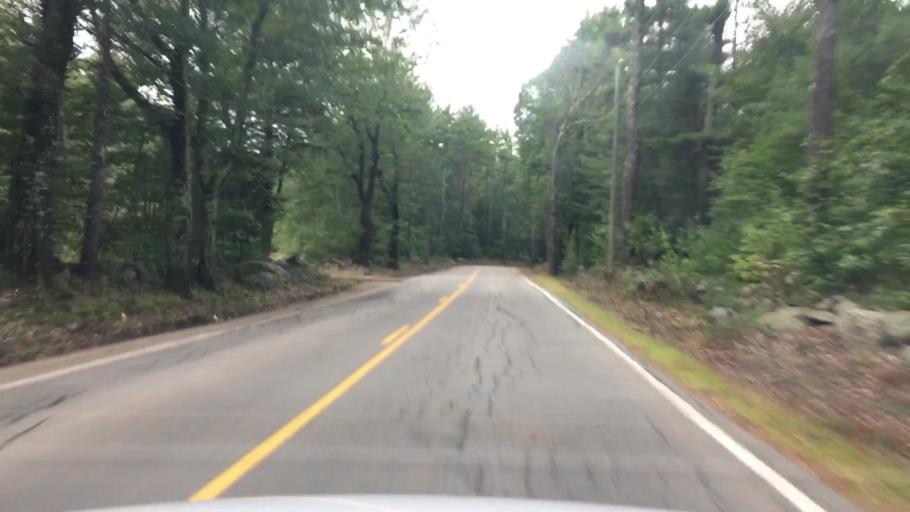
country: US
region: New Hampshire
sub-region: Carroll County
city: Effingham
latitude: 43.7722
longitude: -70.9987
